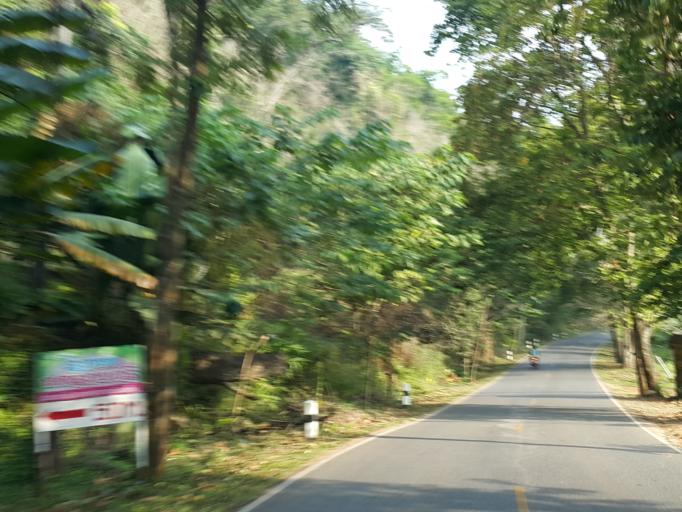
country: TH
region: Chiang Mai
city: Samoeng
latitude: 18.9138
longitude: 98.8244
